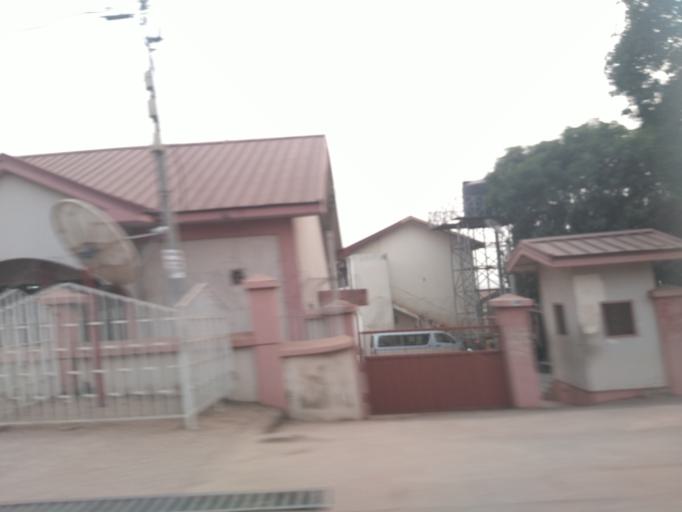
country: GH
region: Ashanti
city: Kumasi
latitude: 6.6837
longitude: -1.6167
